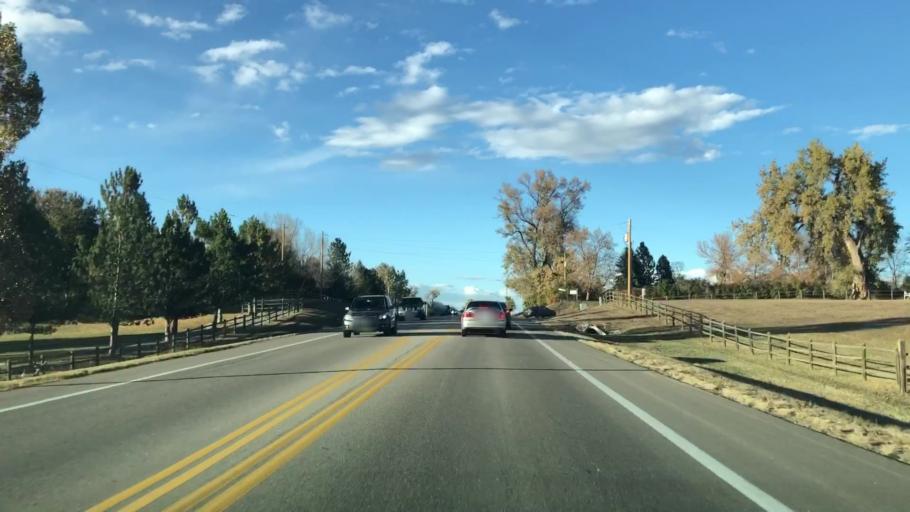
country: US
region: Colorado
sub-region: Larimer County
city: Loveland
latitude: 40.4902
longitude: -105.0393
